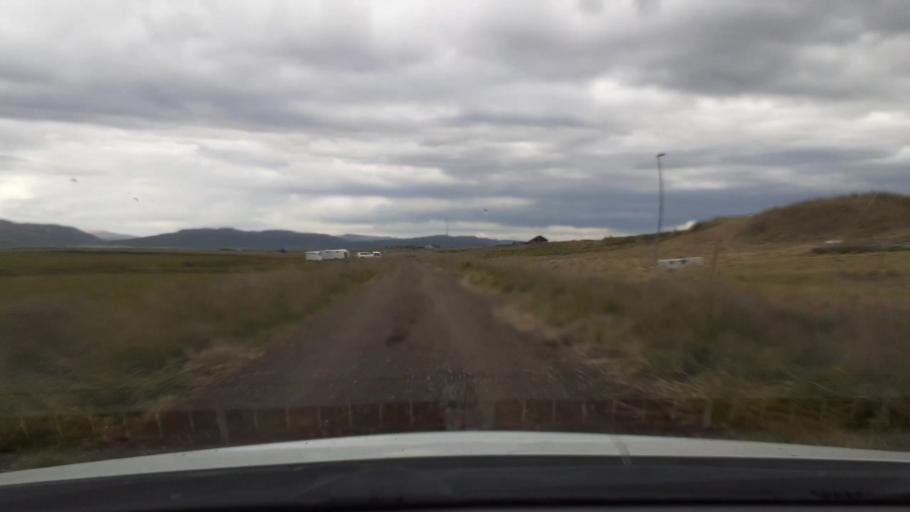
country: IS
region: West
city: Borgarnes
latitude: 64.6526
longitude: -21.8807
